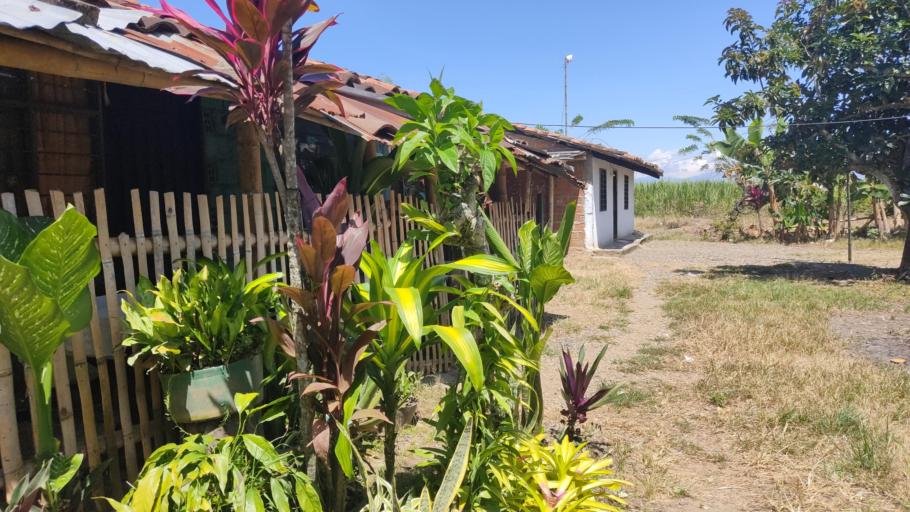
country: CO
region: Valle del Cauca
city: Jamundi
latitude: 3.1548
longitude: -76.5093
